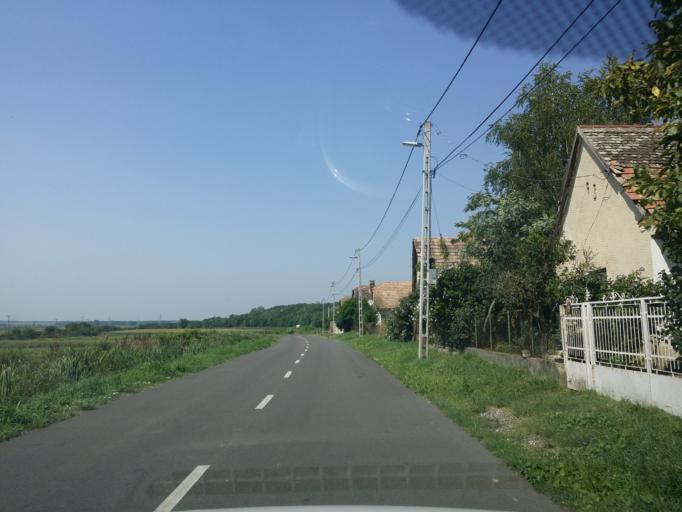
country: HU
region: Tolna
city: Pincehely
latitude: 46.6120
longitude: 18.4211
